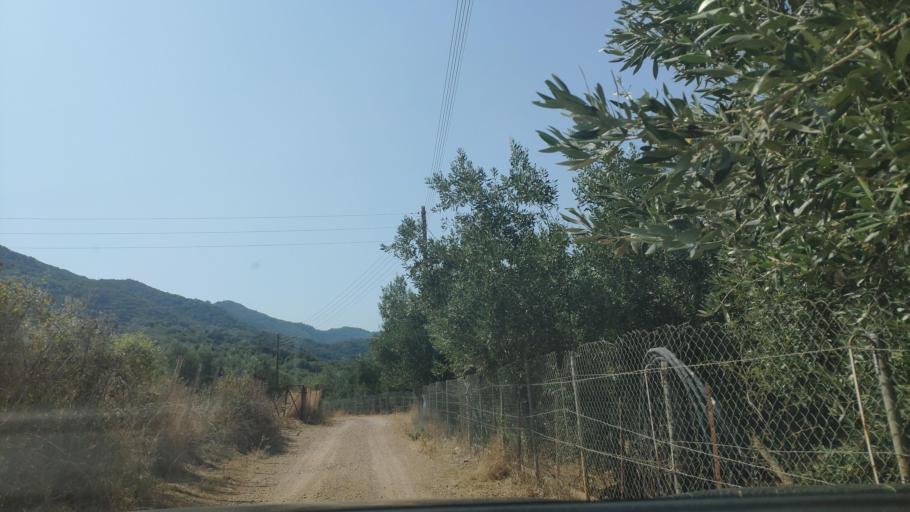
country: GR
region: West Greece
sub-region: Nomos Aitolias kai Akarnanias
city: Fitiai
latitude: 38.7221
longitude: 21.1932
